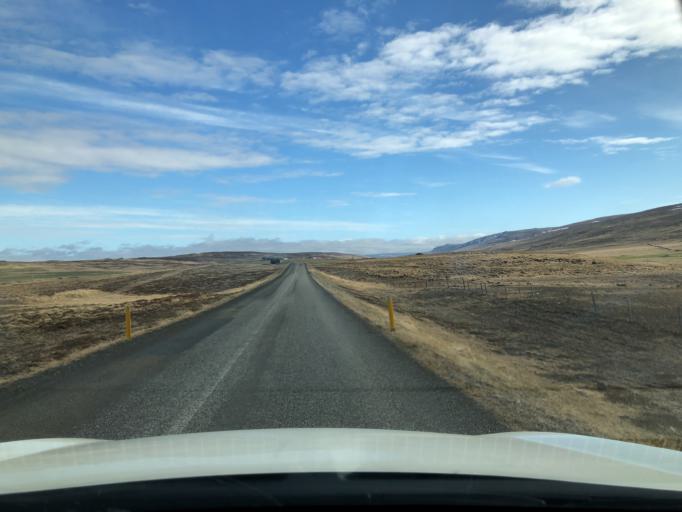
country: IS
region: West
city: Borgarnes
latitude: 65.1047
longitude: -21.7068
